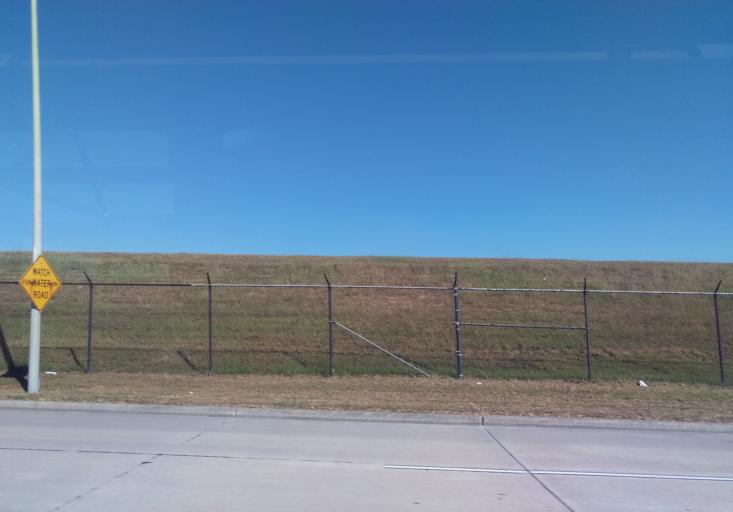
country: US
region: Texas
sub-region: Harris County
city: Aldine
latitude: 29.9813
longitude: -95.3321
